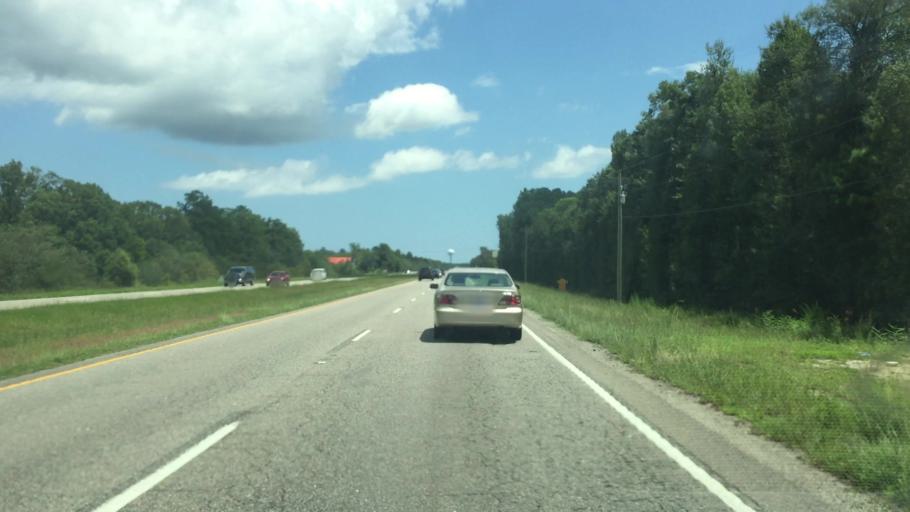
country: US
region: South Carolina
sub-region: Horry County
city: North Myrtle Beach
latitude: 33.9151
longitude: -78.7193
